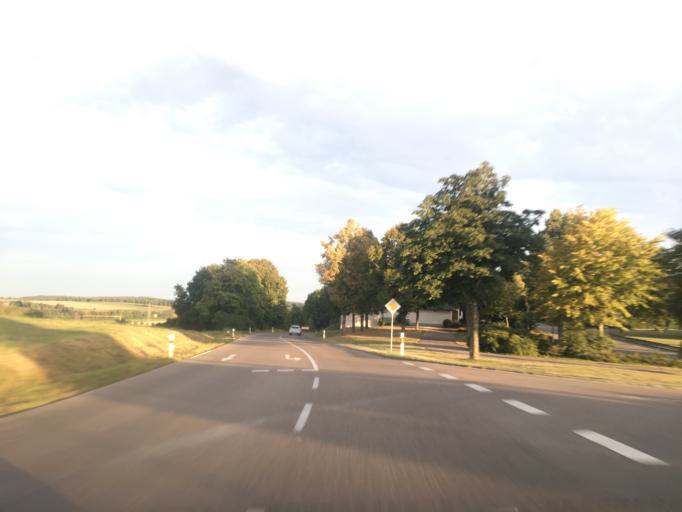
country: DE
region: Baden-Wuerttemberg
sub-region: Tuebingen Region
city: Hayingen
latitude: 48.2809
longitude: 9.4723
